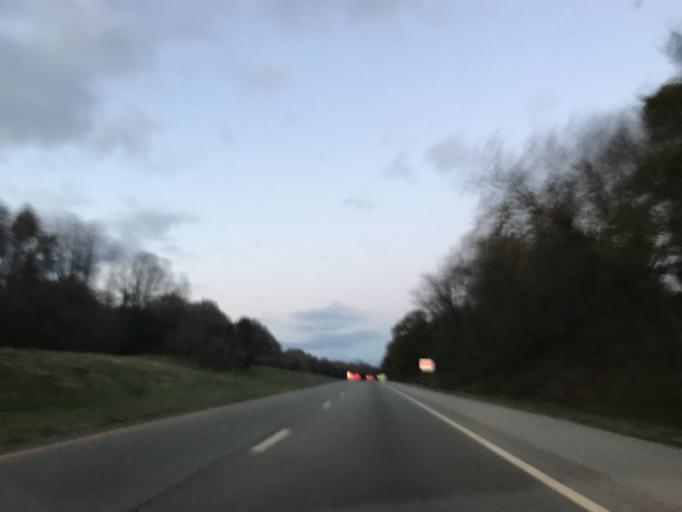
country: US
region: Delaware
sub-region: New Castle County
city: Claymont
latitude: 39.7937
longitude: -75.4890
